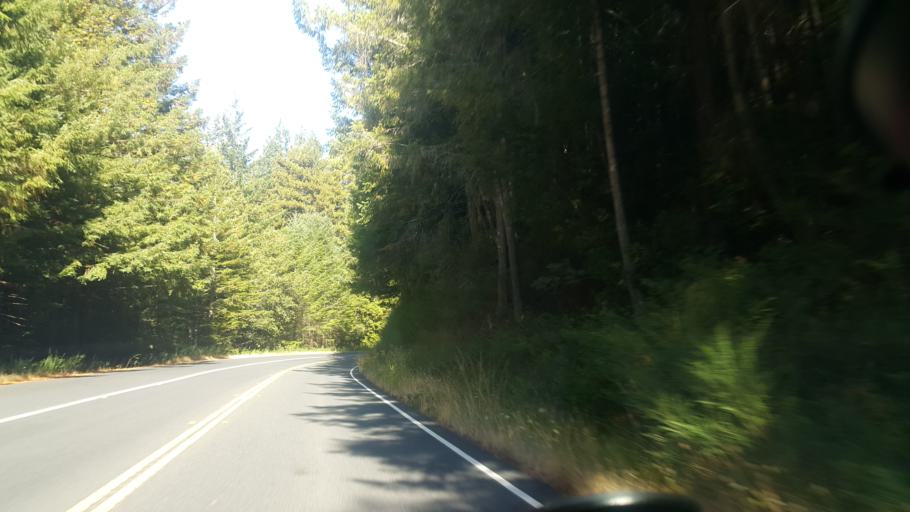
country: US
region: California
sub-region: Mendocino County
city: Fort Bragg
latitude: 39.3616
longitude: -123.6630
